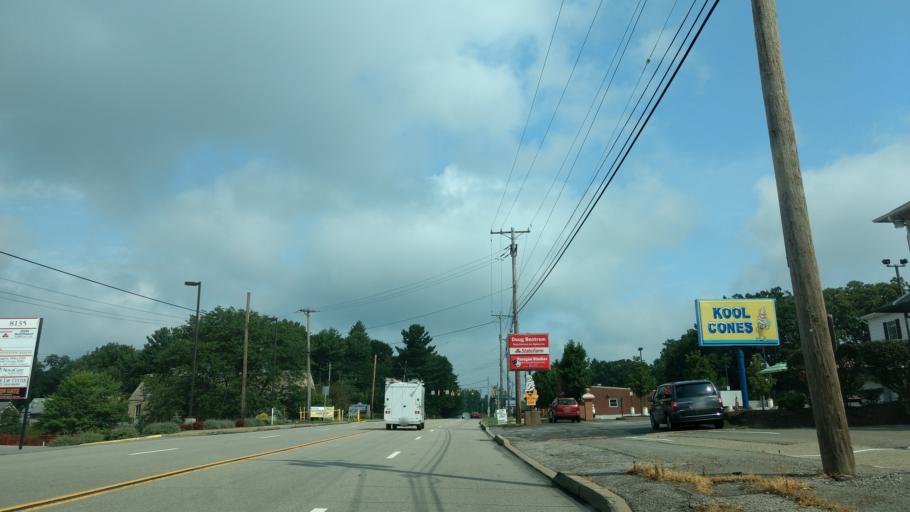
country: US
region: Pennsylvania
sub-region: Allegheny County
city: West View
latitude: 40.5550
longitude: -80.0387
